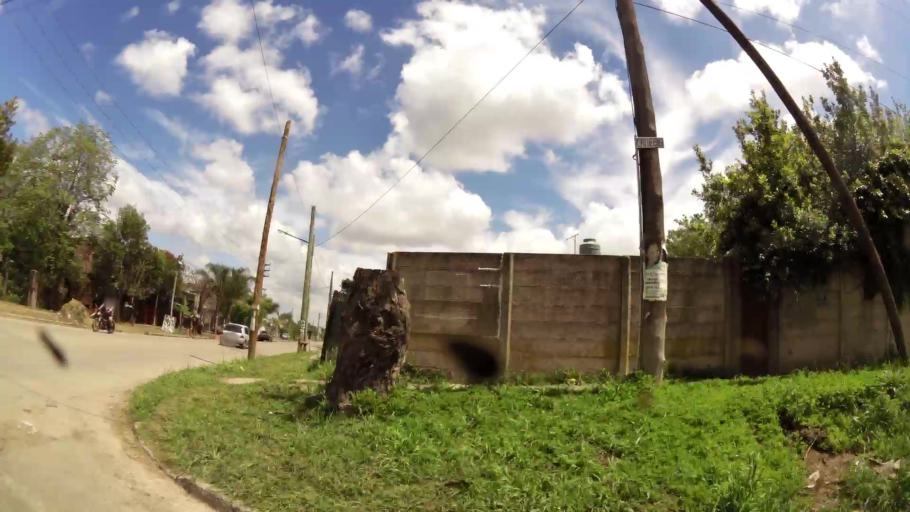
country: AR
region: Buenos Aires
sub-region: Partido de Quilmes
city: Quilmes
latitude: -34.8200
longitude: -58.2404
